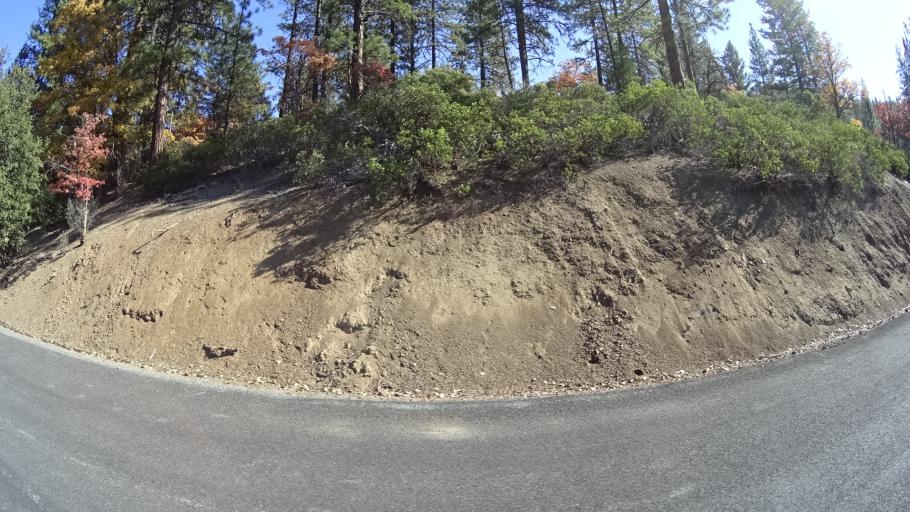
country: US
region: California
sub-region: Siskiyou County
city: Yreka
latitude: 41.6781
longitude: -122.8483
